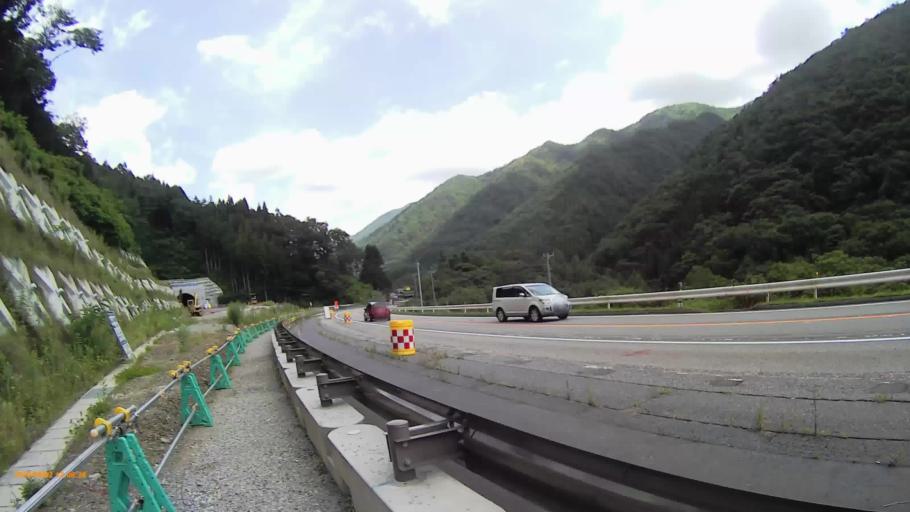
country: JP
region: Nagano
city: Shiojiri
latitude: 36.0270
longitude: 137.8713
